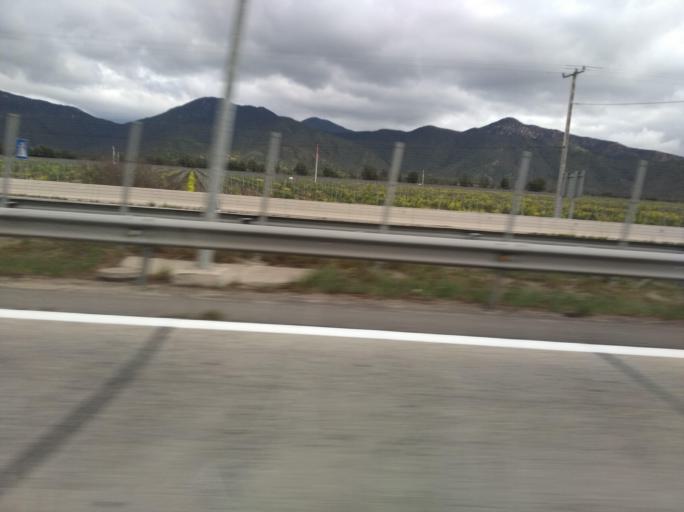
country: CL
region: Valparaiso
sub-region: Provincia de Marga Marga
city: Villa Alemana
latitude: -33.3654
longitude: -71.3110
